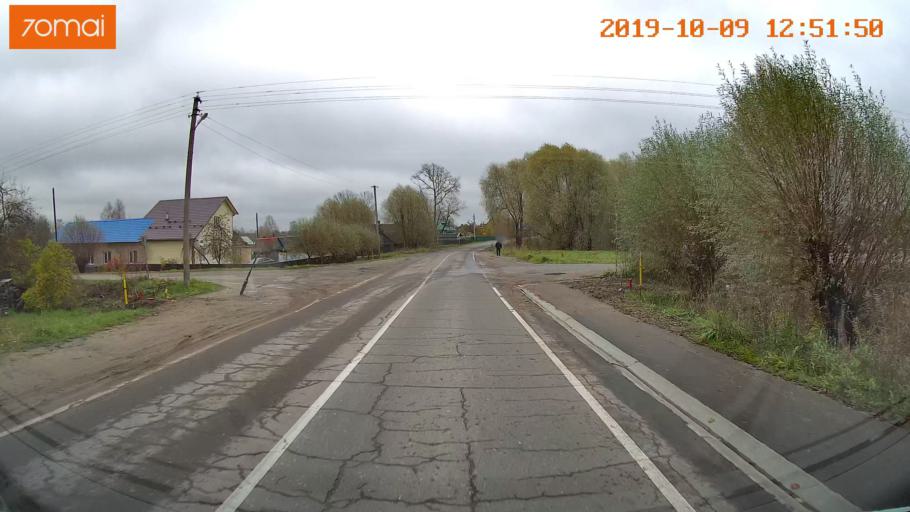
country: RU
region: Jaroslavl
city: Prechistoye
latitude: 58.4173
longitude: 40.3472
